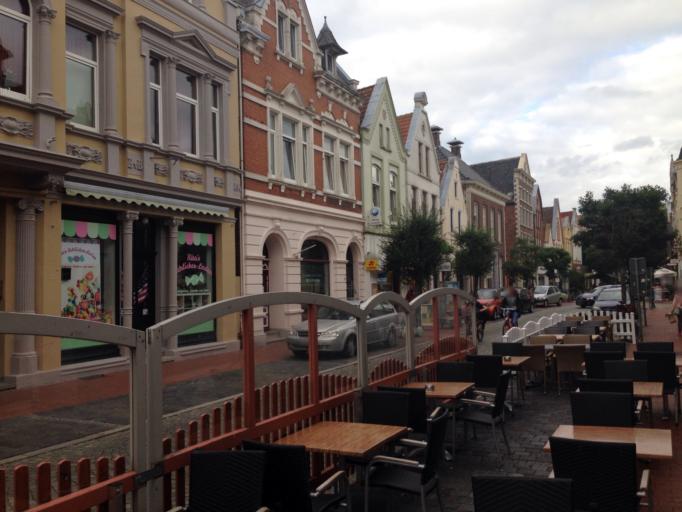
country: DE
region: Lower Saxony
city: Leer
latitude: 53.2297
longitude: 7.4528
